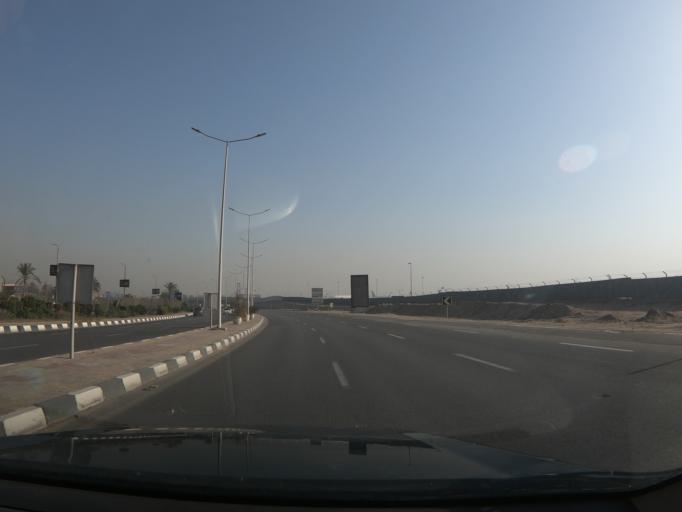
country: EG
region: Muhafazat al Qalyubiyah
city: Al Khankah
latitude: 30.1023
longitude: 31.3878
